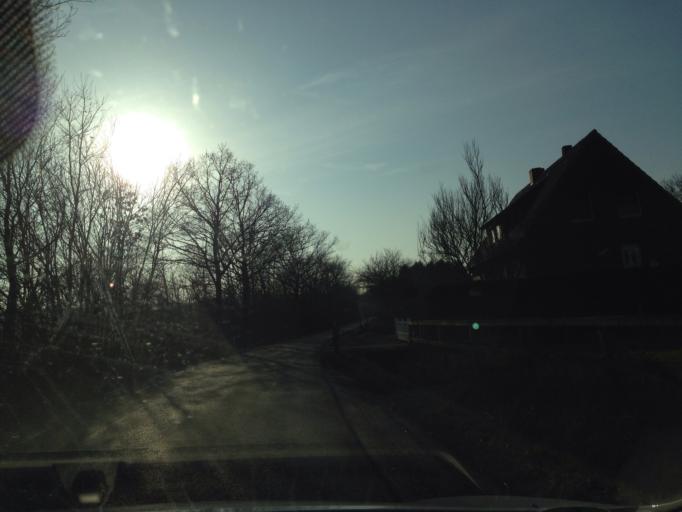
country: DE
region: North Rhine-Westphalia
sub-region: Regierungsbezirk Munster
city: Muenster
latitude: 52.0172
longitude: 7.5721
